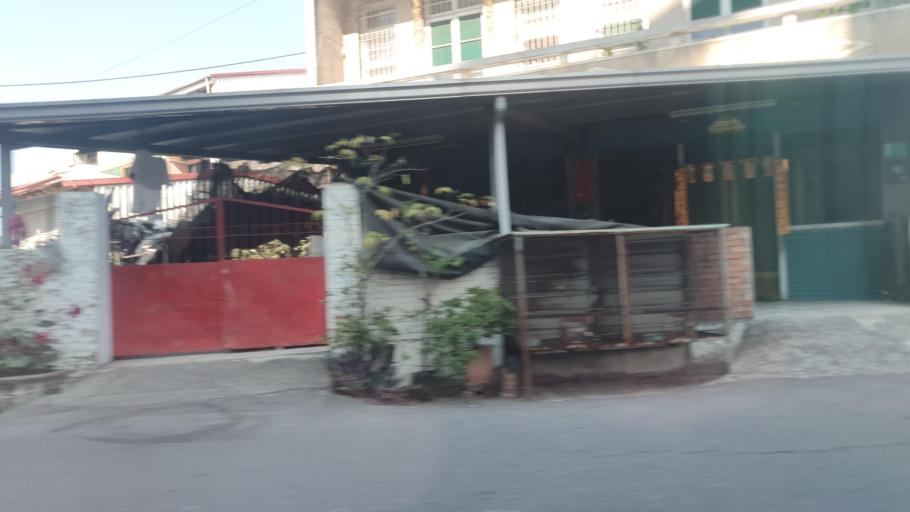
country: TW
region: Taiwan
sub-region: Tainan
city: Tainan
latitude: 23.0345
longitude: 120.2996
